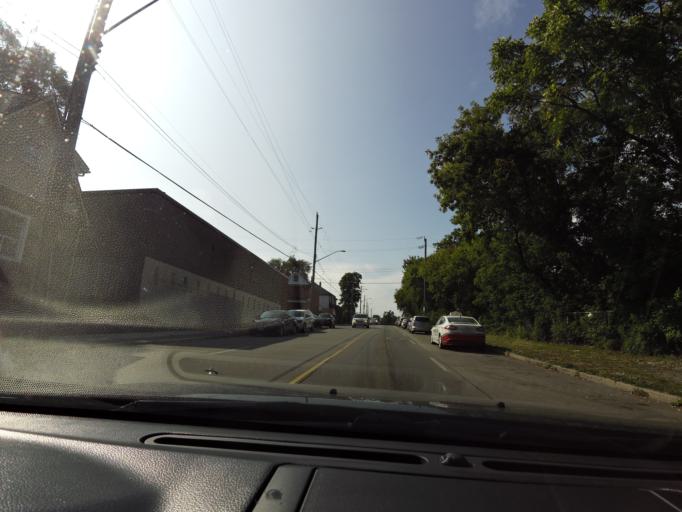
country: CA
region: Ontario
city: Hamilton
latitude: 43.2666
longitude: -79.8764
